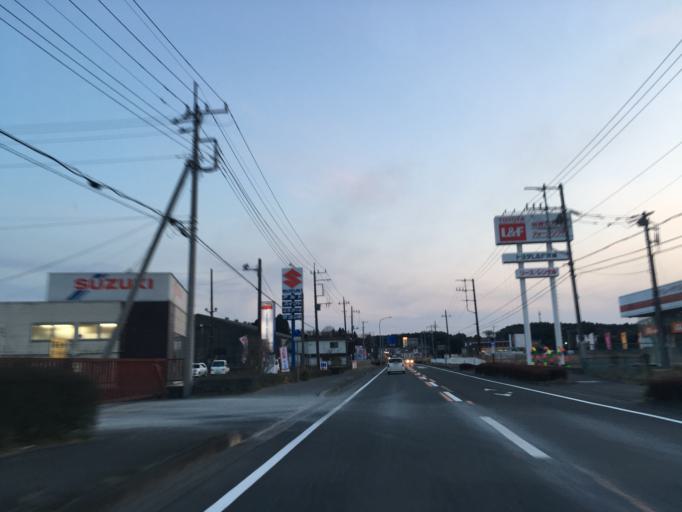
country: JP
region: Ibaraki
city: Takahagi
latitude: 36.7468
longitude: 140.7283
